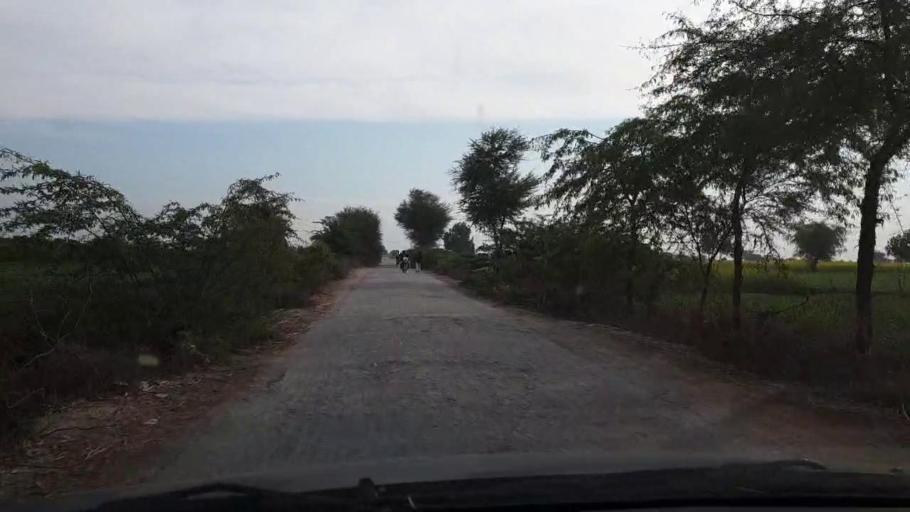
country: PK
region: Sindh
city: Khadro
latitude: 26.1207
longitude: 68.7961
